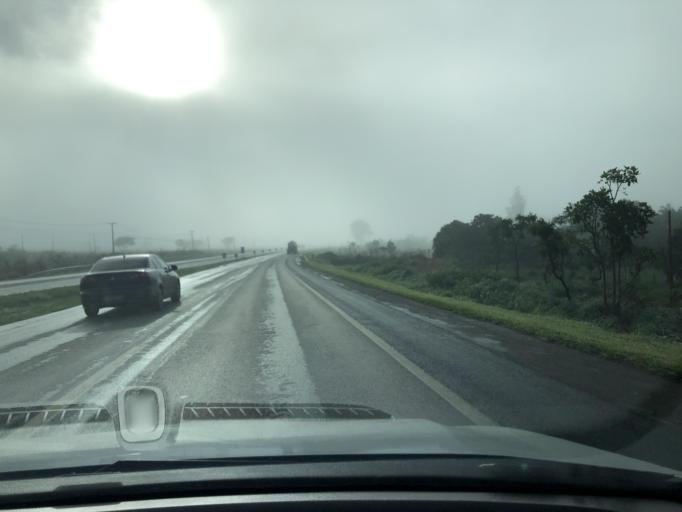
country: BR
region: Goias
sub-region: Luziania
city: Luziania
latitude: -16.2769
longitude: -47.8643
